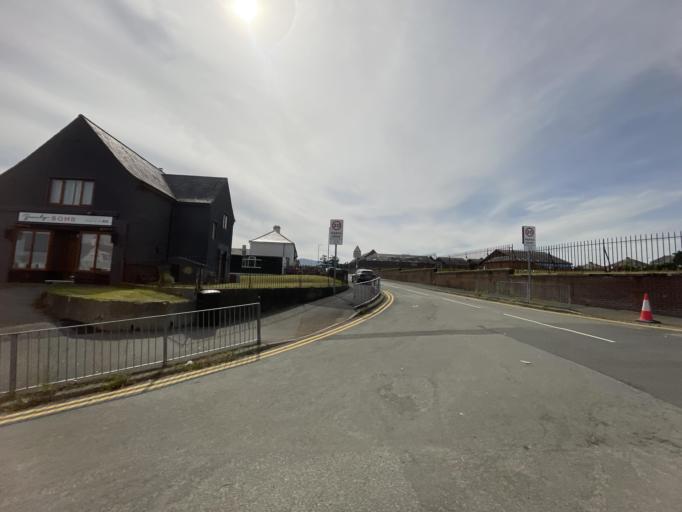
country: GB
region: Wales
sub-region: Gwynedd
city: Bangor
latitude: 53.2216
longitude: -4.1461
